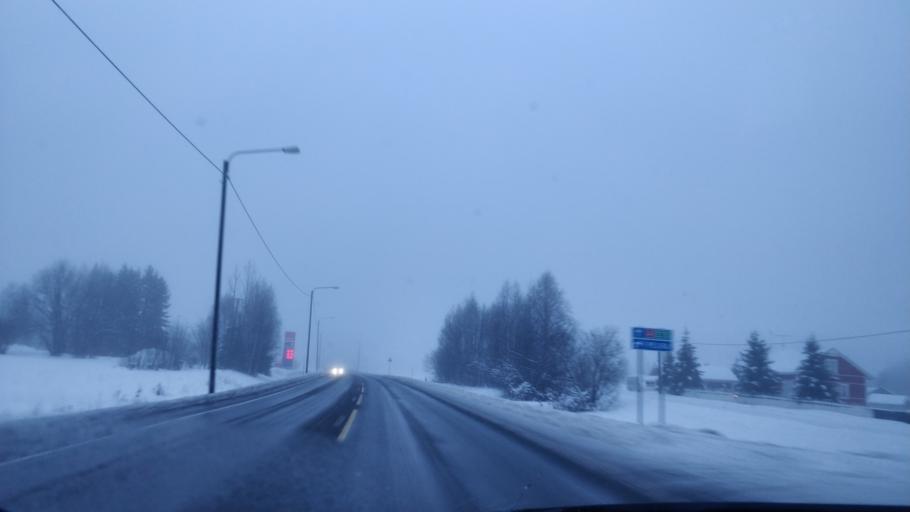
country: FI
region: Lapland
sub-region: Kemi-Tornio
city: Tervola
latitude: 66.1437
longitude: 24.9579
